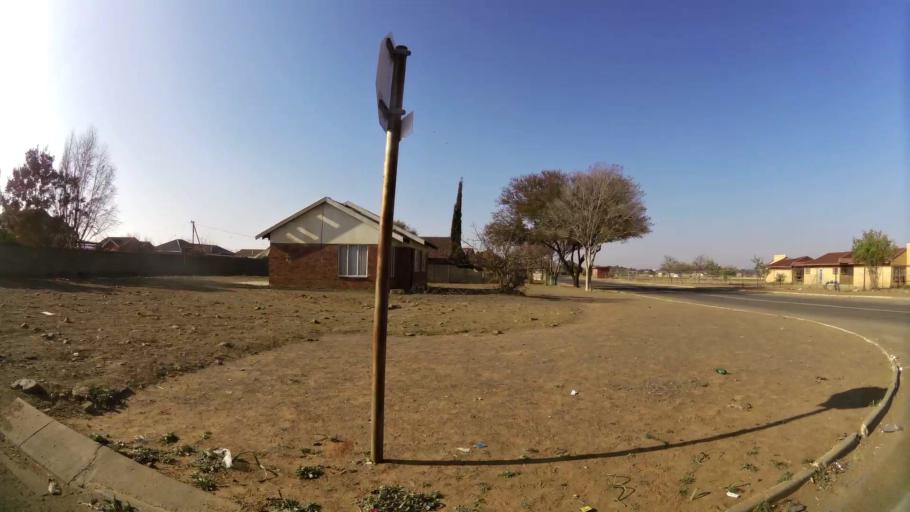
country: ZA
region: Orange Free State
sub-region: Mangaung Metropolitan Municipality
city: Bloemfontein
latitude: -29.1796
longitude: 26.1781
